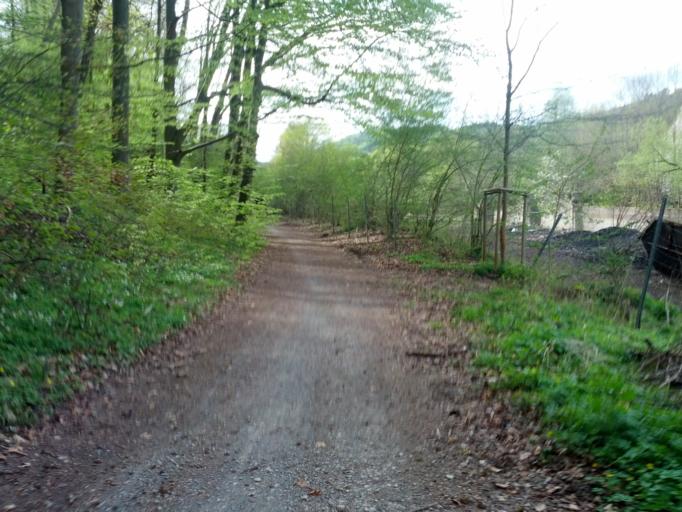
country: DE
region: Thuringia
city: Krauthausen
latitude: 51.0058
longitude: 10.2378
